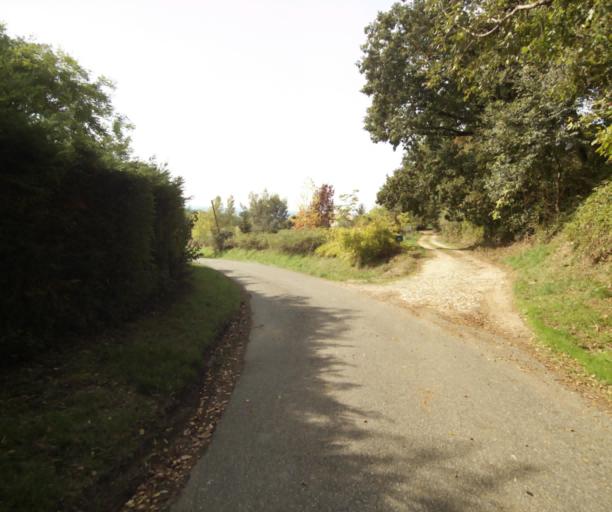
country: FR
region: Midi-Pyrenees
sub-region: Departement du Tarn-et-Garonne
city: Corbarieu
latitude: 43.9649
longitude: 1.3802
